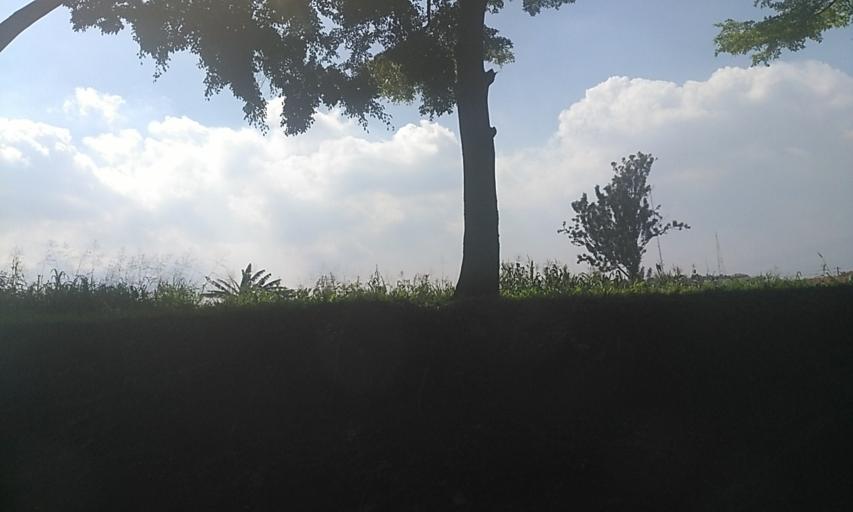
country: UG
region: Central Region
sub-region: Wakiso District
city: Kireka
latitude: 0.3402
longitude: 32.6152
